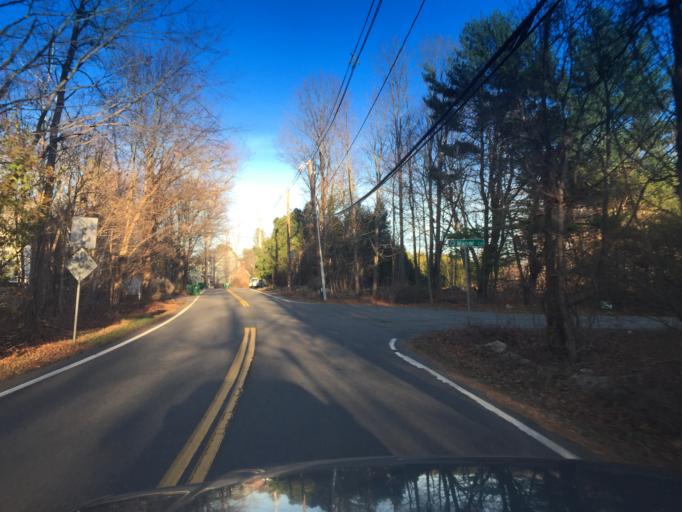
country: US
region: Massachusetts
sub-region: Norfolk County
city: Westwood
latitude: 42.2171
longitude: -71.2057
